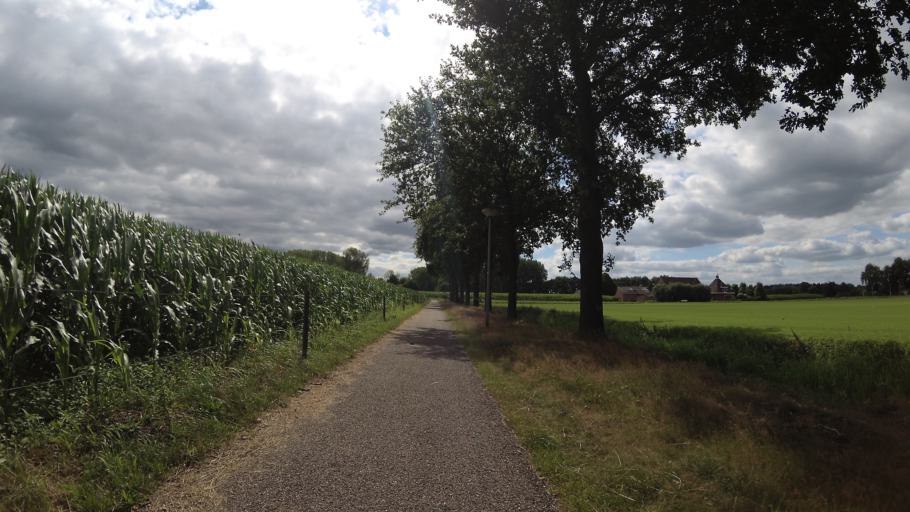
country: NL
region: North Brabant
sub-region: Gemeente Dongen
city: Dongen
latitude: 51.6381
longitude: 4.9091
